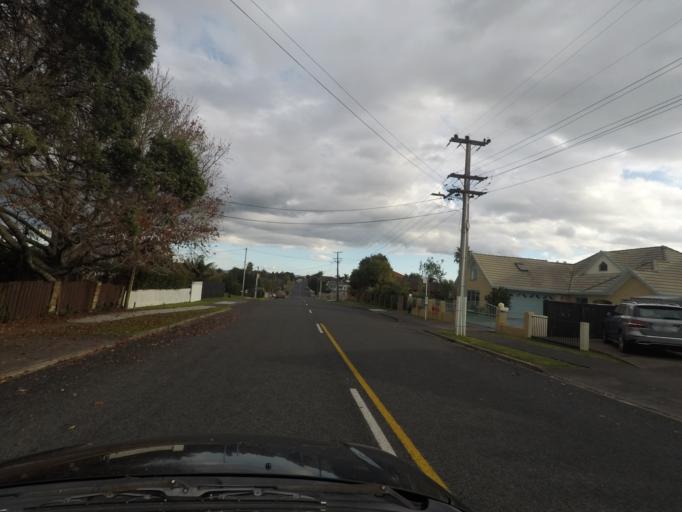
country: NZ
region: Auckland
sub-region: Auckland
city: Rosebank
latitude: -36.8015
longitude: 174.6461
